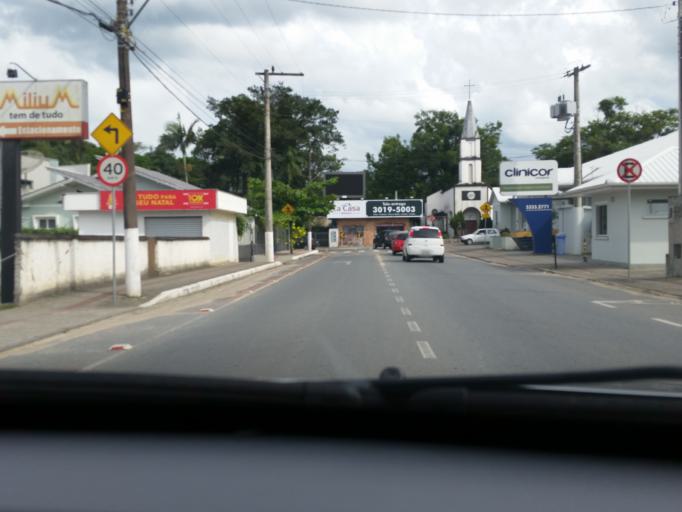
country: BR
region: Santa Catarina
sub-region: Indaial
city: Indaial
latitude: -26.8936
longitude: -49.2411
